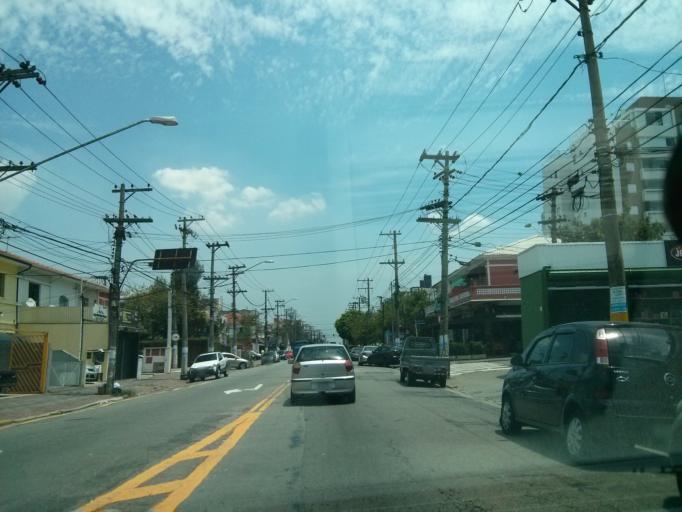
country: BR
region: Sao Paulo
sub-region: Sao Paulo
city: Sao Paulo
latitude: -23.6061
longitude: -46.6163
